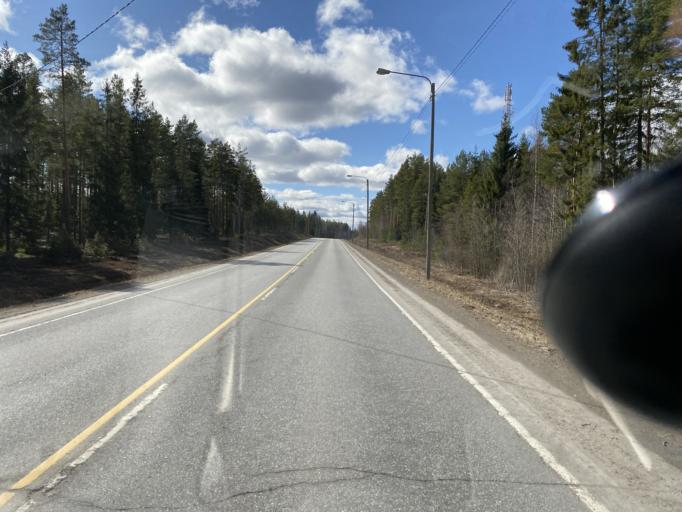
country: FI
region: Satakunta
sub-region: Rauma
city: Eura
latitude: 61.1406
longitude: 22.1868
